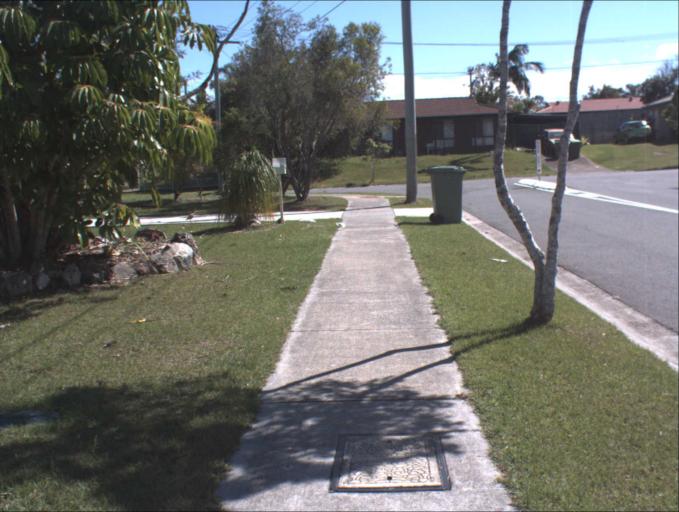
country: AU
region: Queensland
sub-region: Logan
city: Logan Reserve
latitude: -27.6899
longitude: 153.0844
